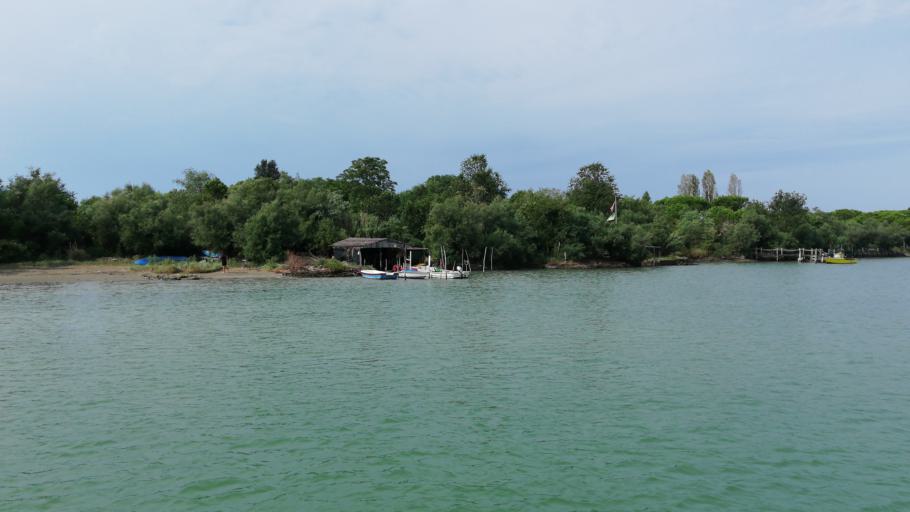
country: IT
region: Veneto
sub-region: Provincia di Venezia
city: Caorle
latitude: 45.6207
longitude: 12.9075
